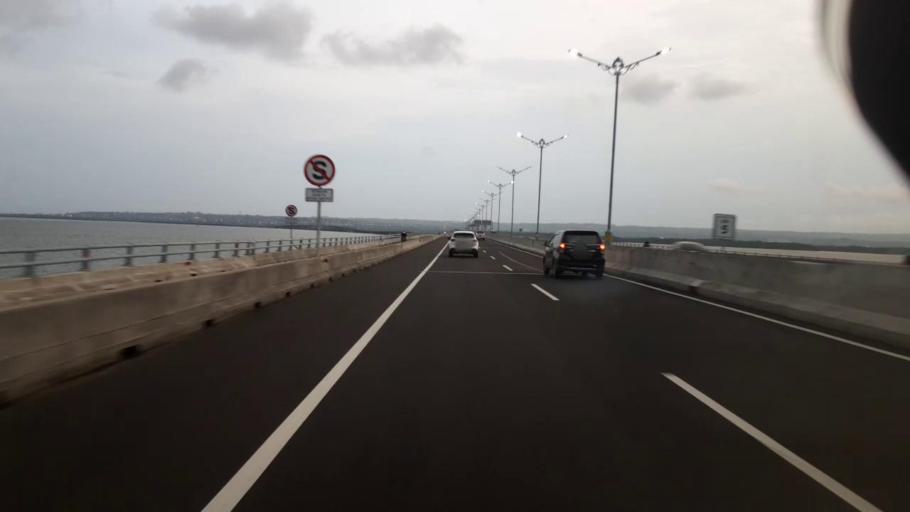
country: ID
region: Bali
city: Kelanabian
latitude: -8.7515
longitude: 115.1955
